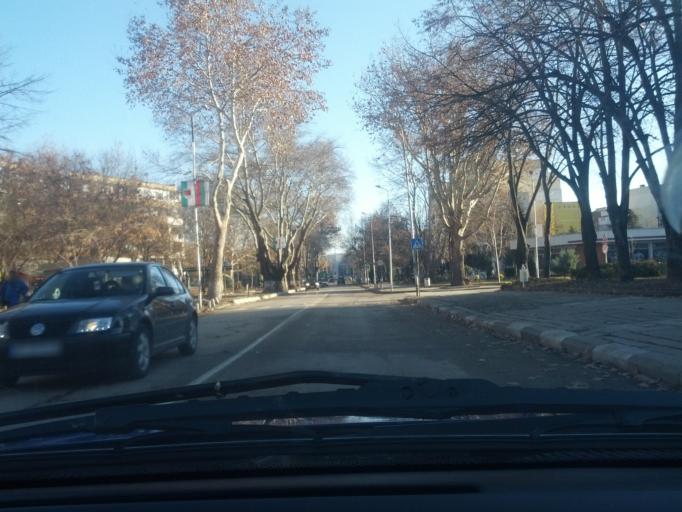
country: BG
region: Vratsa
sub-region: Obshtina Kozloduy
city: Kozloduy
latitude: 43.7809
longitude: 23.7237
